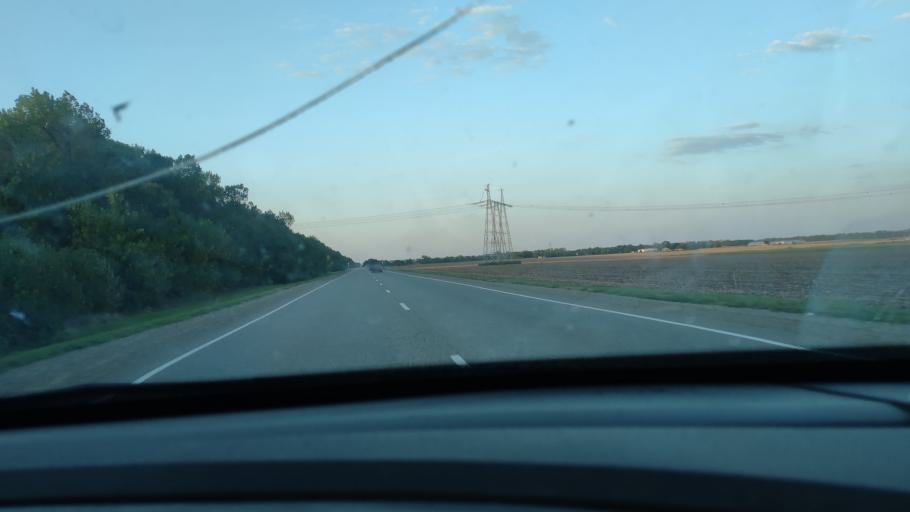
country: RU
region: Krasnodarskiy
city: Novominskaya
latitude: 46.3998
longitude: 38.9962
